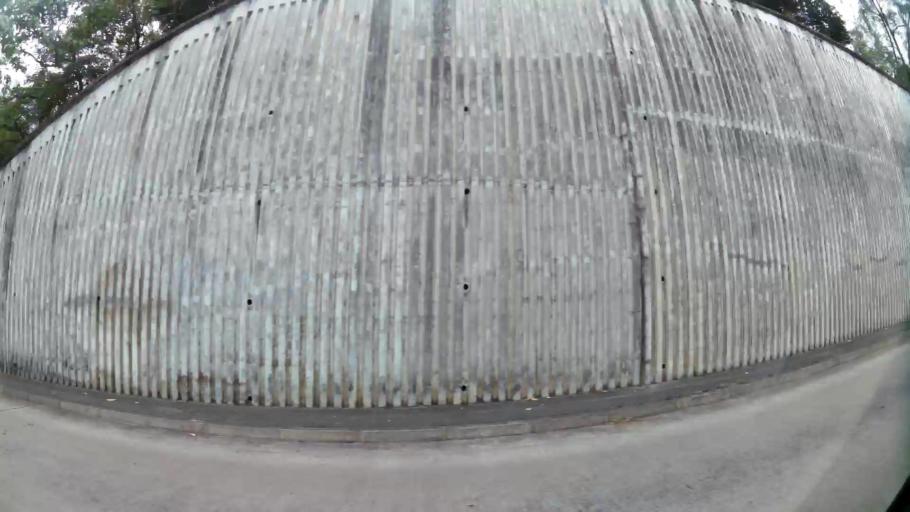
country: HK
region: Wanchai
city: Wan Chai
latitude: 22.2652
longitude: 114.2377
